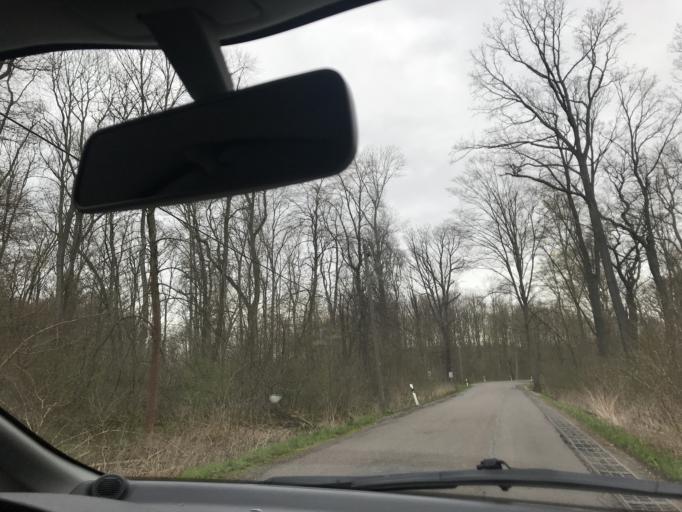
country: DE
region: Saxony
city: Schkeuditz
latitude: 51.3695
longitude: 12.2567
